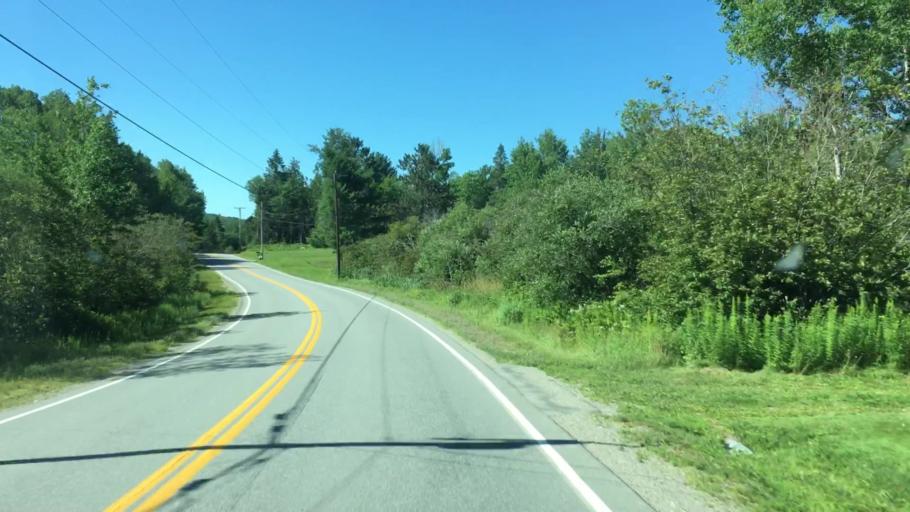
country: US
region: Maine
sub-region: Hancock County
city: Dedham
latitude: 44.7091
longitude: -68.6499
